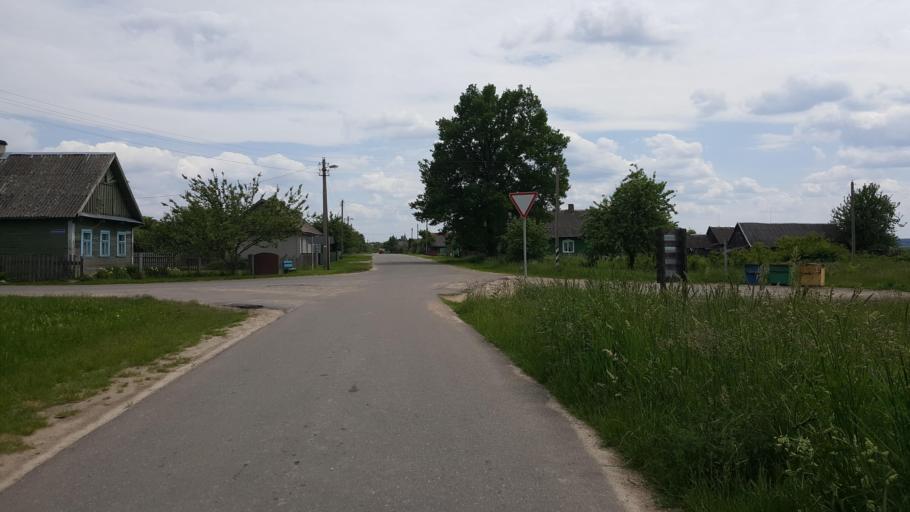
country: PL
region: Podlasie
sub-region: Powiat hajnowski
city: Bialowieza
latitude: 52.6676
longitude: 24.0777
